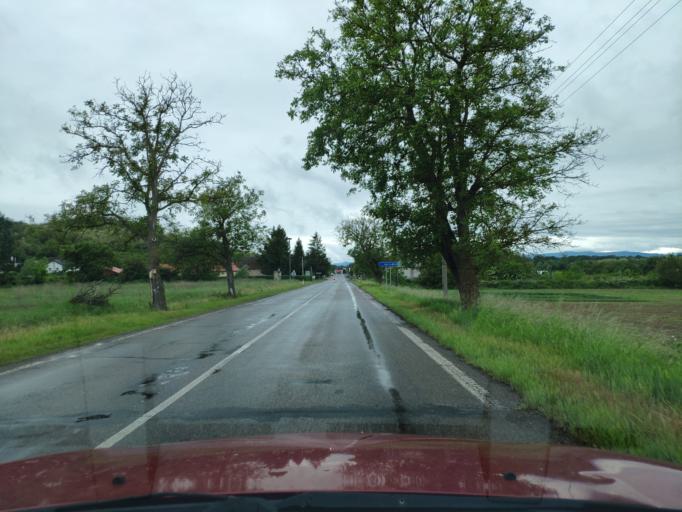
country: HU
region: Borsod-Abauj-Zemplen
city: Ricse
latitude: 48.4360
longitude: 21.9305
